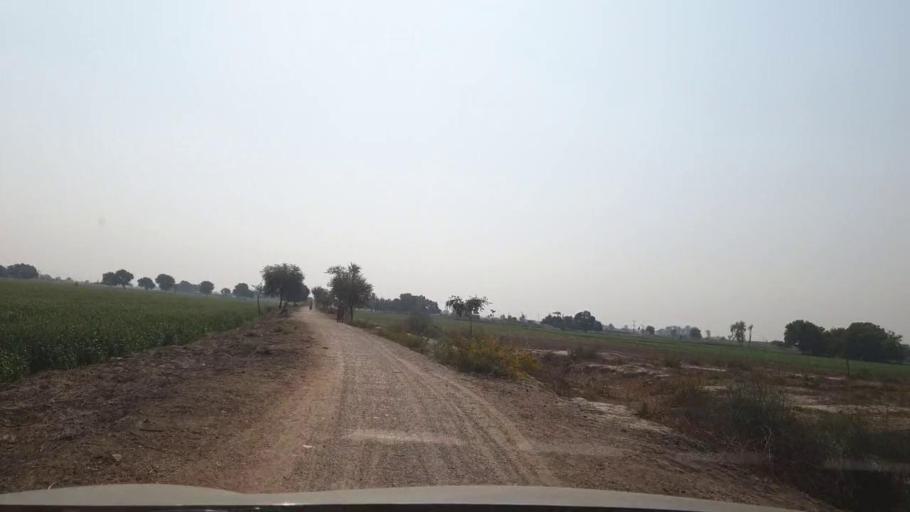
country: PK
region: Sindh
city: Tando Allahyar
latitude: 25.5380
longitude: 68.8342
